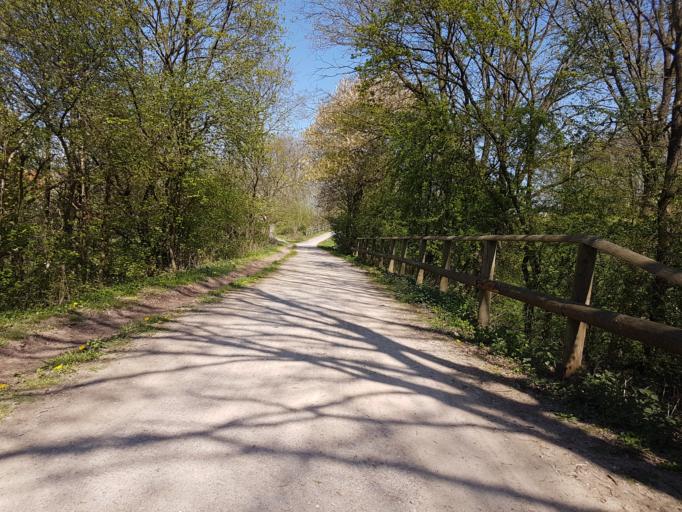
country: DE
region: North Rhine-Westphalia
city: Gevelsberg
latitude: 51.3566
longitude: 7.3277
